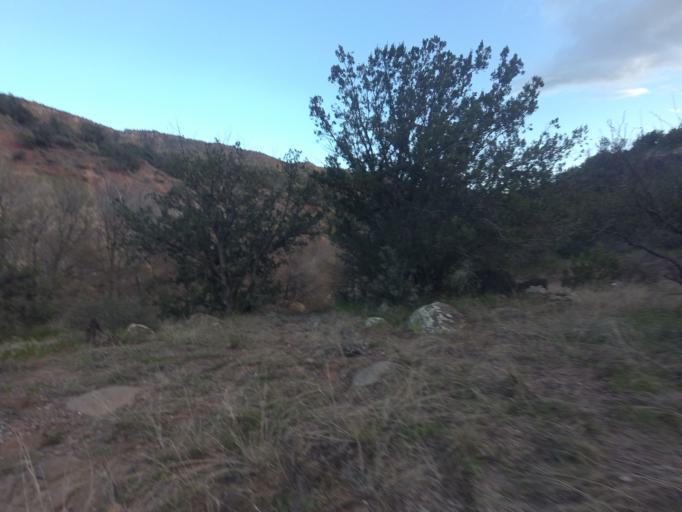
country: US
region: Arizona
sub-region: Gila County
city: Pine
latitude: 34.3794
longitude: -111.6589
